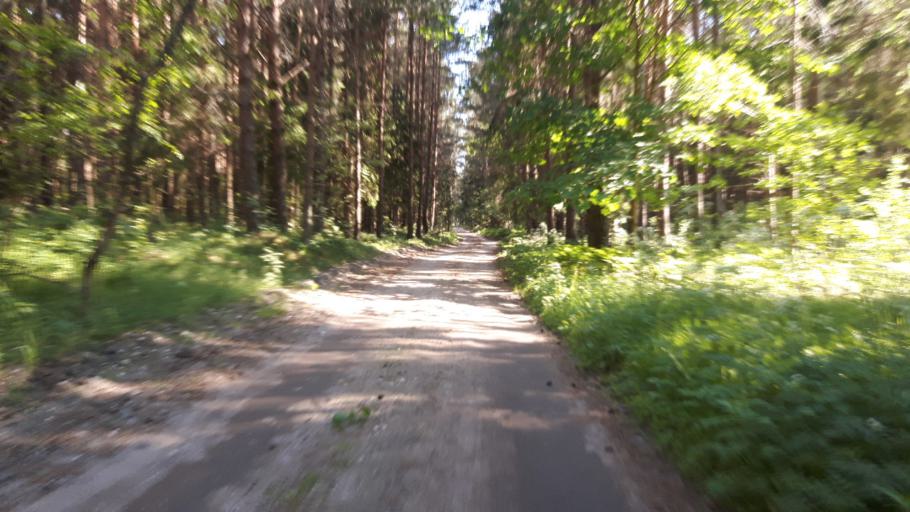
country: LV
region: Salacgrivas
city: Salacgriva
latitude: 57.7351
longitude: 24.3503
